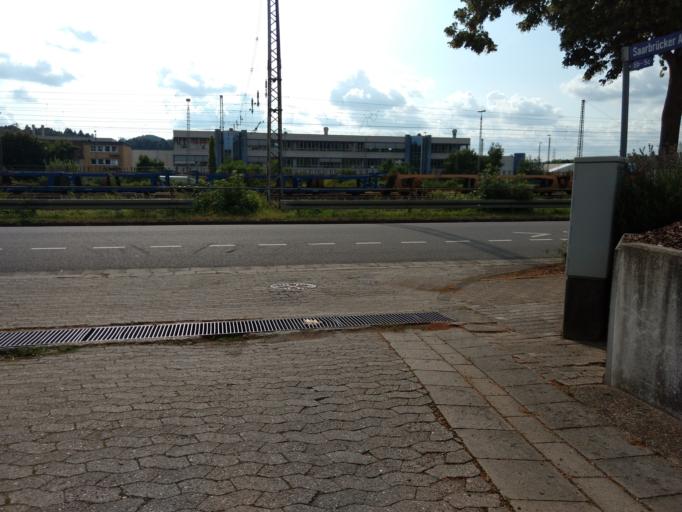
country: DE
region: Saarland
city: Merzig
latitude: 49.4343
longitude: 6.6348
